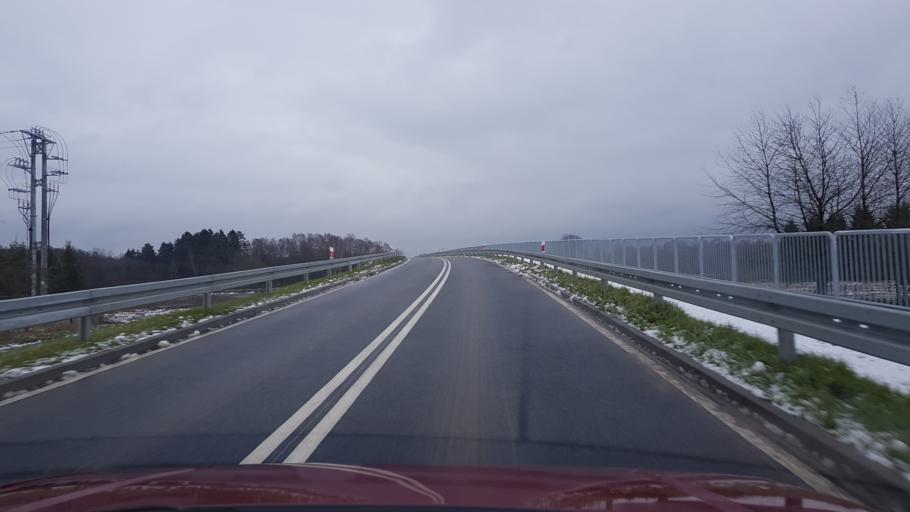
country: PL
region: West Pomeranian Voivodeship
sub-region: Powiat gryficki
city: Ploty
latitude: 53.8568
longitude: 15.3406
